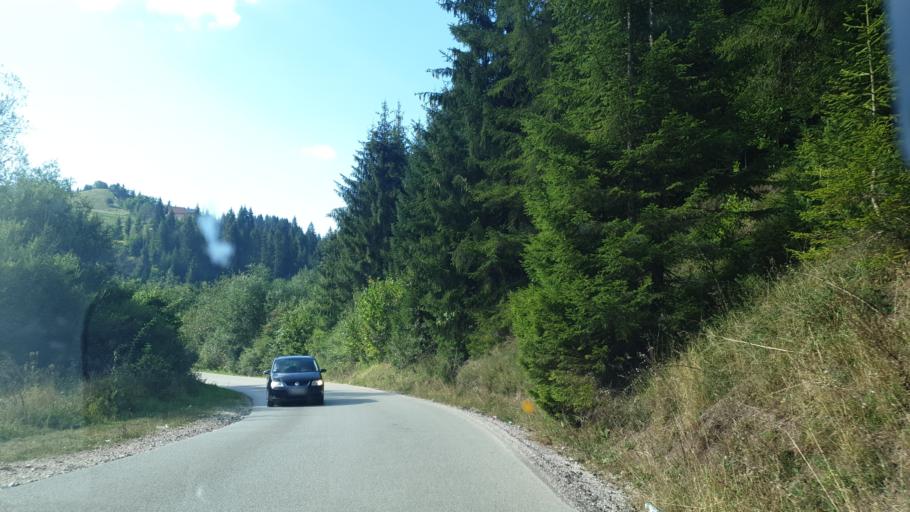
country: RS
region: Central Serbia
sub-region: Zlatiborski Okrug
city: Nova Varos
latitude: 43.4504
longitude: 19.8449
